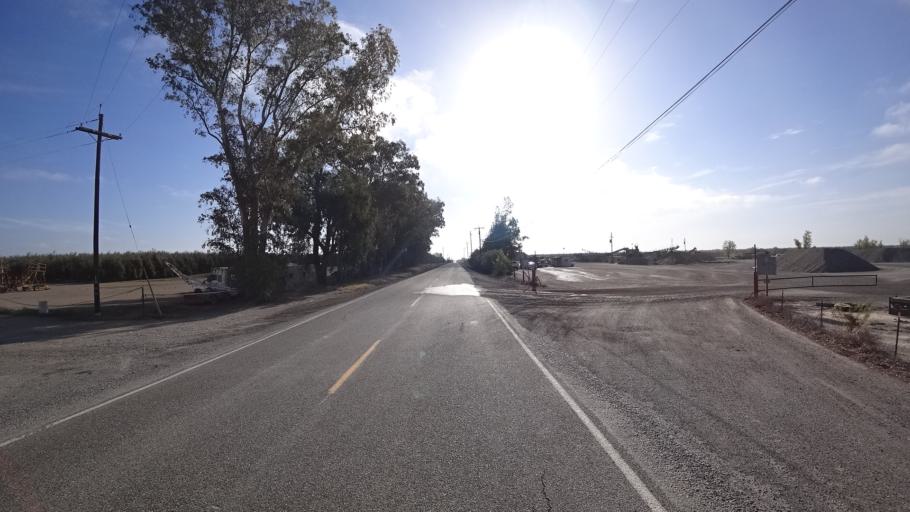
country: US
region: California
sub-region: Glenn County
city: Willows
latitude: 39.5823
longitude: -122.1609
